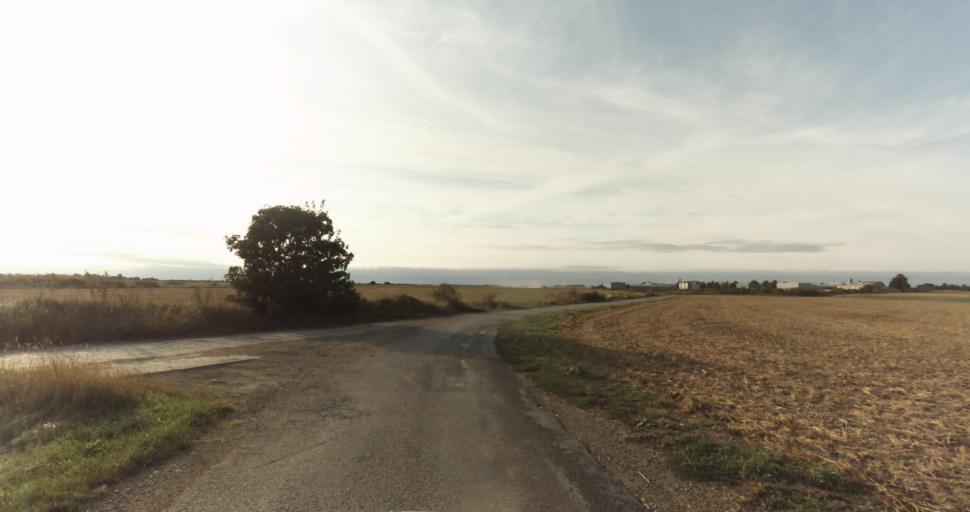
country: FR
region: Haute-Normandie
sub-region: Departement de l'Eure
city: Marcilly-sur-Eure
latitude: 48.8897
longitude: 1.2736
